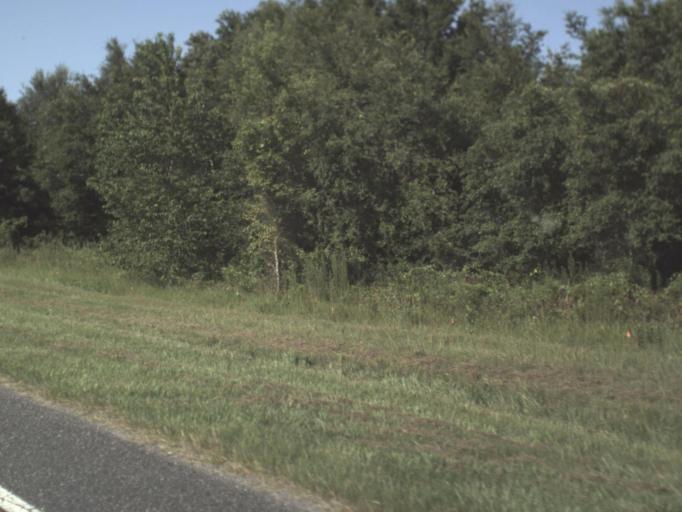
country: US
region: Florida
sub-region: Columbia County
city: Lake City
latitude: 30.0029
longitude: -82.7101
